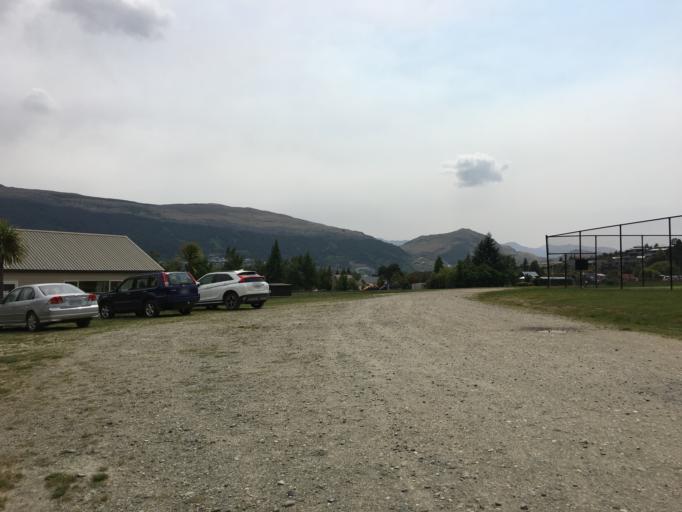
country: NZ
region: Otago
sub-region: Queenstown-Lakes District
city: Queenstown
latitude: -45.0459
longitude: 168.6914
